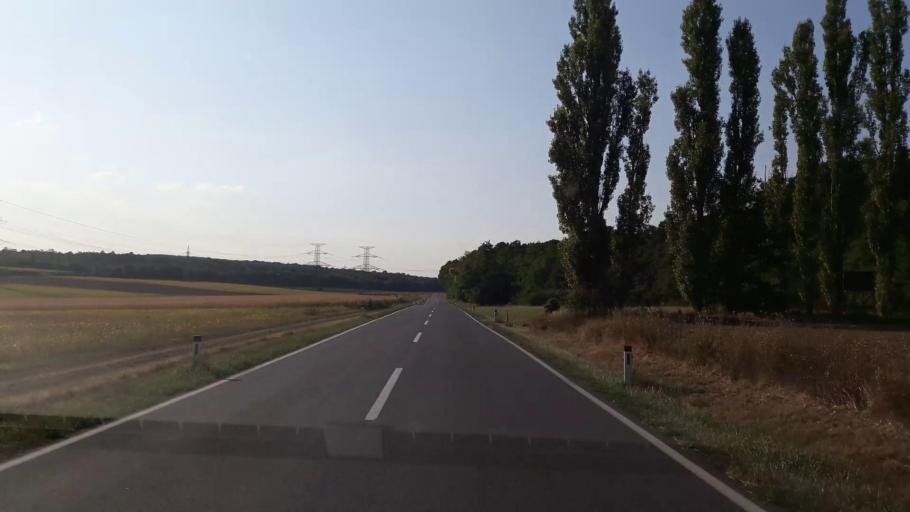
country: AT
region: Lower Austria
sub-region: Politischer Bezirk Ganserndorf
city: Orth an der Donau
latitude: 48.0752
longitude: 16.6890
